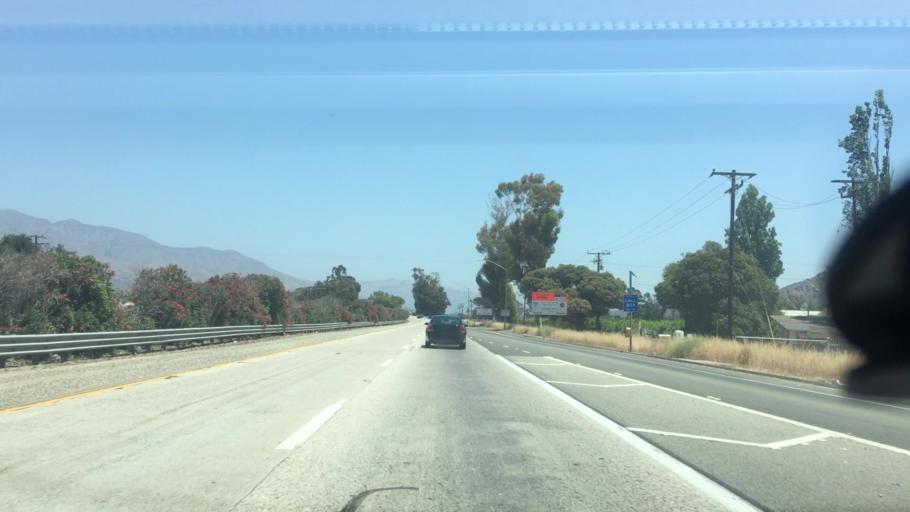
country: US
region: California
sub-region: Ventura County
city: Santa Paula
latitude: 34.3229
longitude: -119.1002
